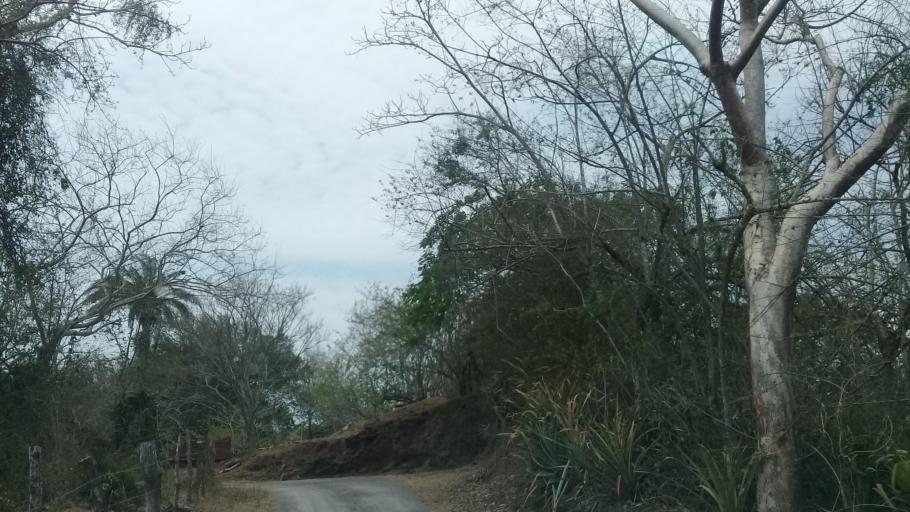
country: MX
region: Veracruz
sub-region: Veracruz
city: Delfino Victoria (Santa Fe)
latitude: 19.1753
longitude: -96.3044
